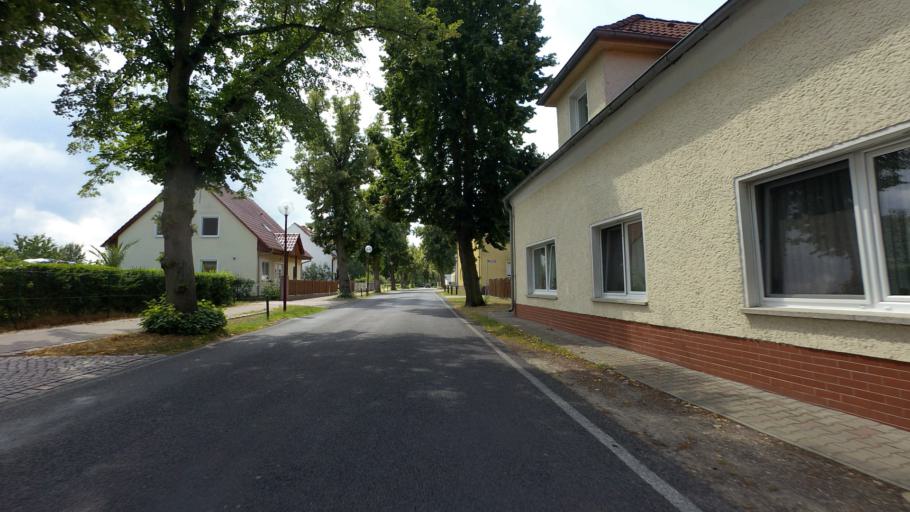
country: DE
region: Brandenburg
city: Teupitz
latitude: 52.1333
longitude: 13.6091
